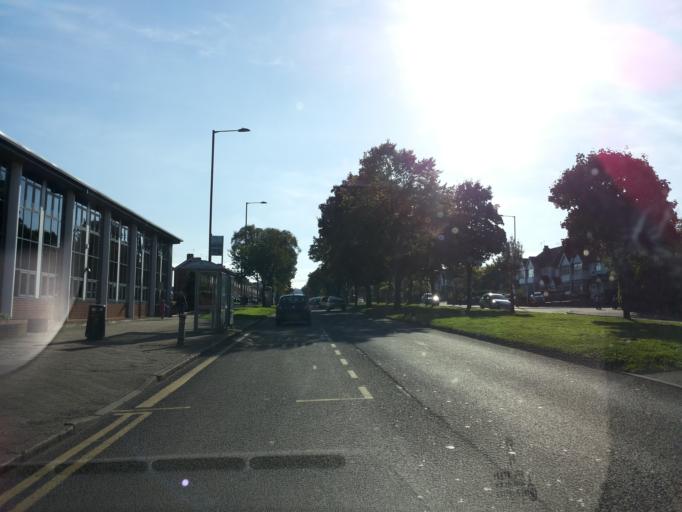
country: GB
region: England
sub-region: City and Borough of Birmingham
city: Bartley Green
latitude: 52.4013
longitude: -1.9826
